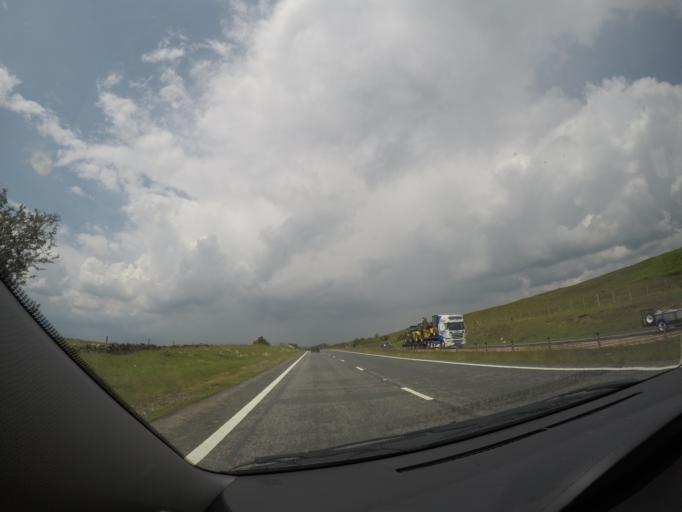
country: GB
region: England
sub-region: Cumbria
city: Appleby-in-Westmorland
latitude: 54.5587
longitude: -2.4387
